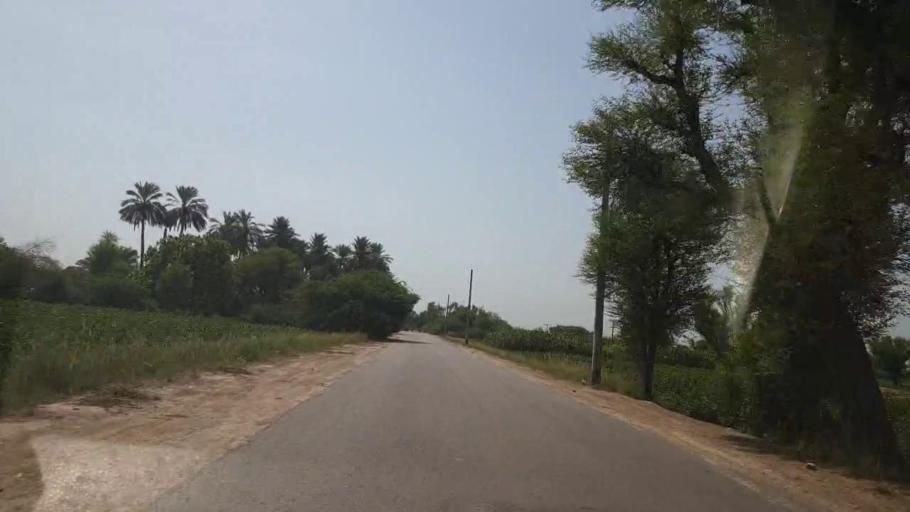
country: PK
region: Sindh
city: Bozdar
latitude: 27.1207
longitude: 68.5490
